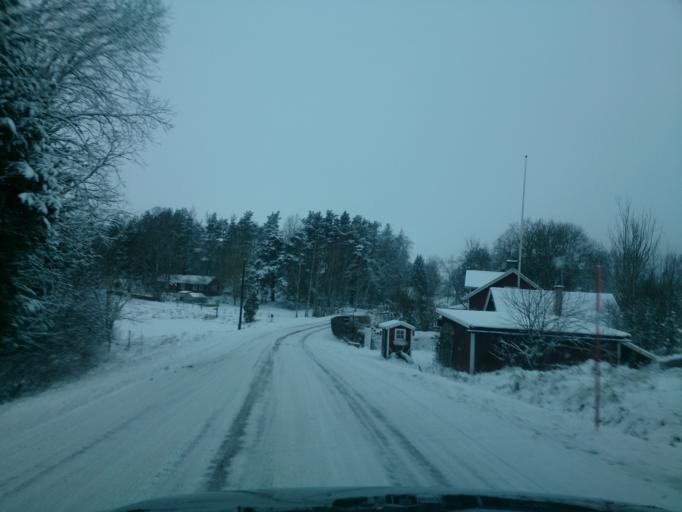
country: SE
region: OEstergoetland
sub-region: Norrkopings Kommun
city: Kimstad
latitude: 58.4224
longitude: 15.9126
